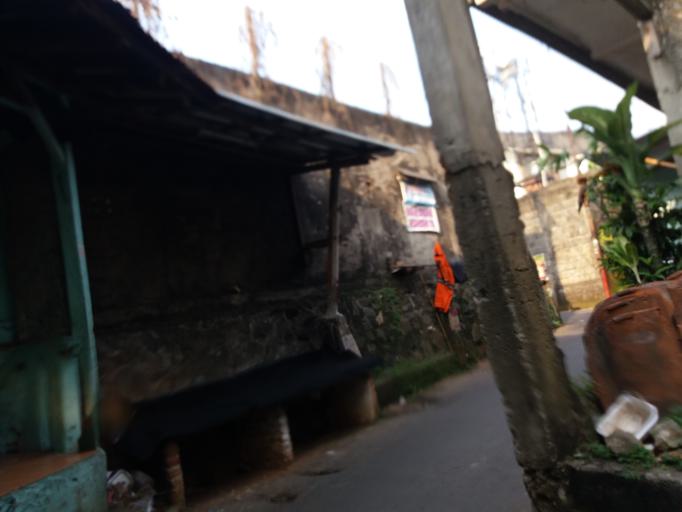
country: ID
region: Jakarta Raya
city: Jakarta
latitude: -6.2438
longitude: 106.8126
